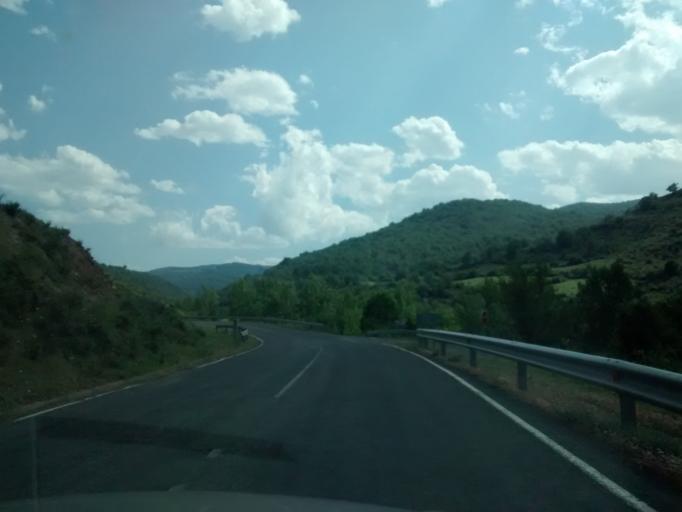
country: ES
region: La Rioja
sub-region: Provincia de La Rioja
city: Rabanera
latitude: 42.1865
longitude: -2.4837
